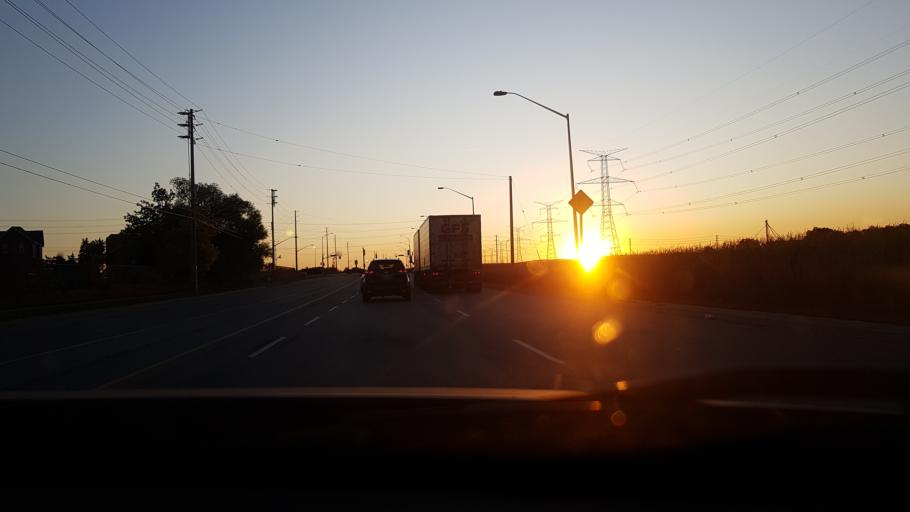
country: CA
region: Ontario
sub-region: Halton
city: Milton
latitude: 43.5475
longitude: -79.8810
